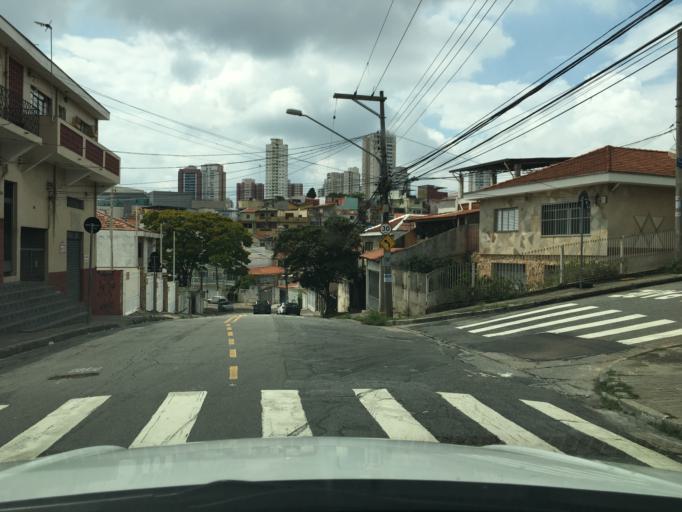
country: BR
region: Sao Paulo
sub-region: Sao Paulo
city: Sao Paulo
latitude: -23.4850
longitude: -46.6481
